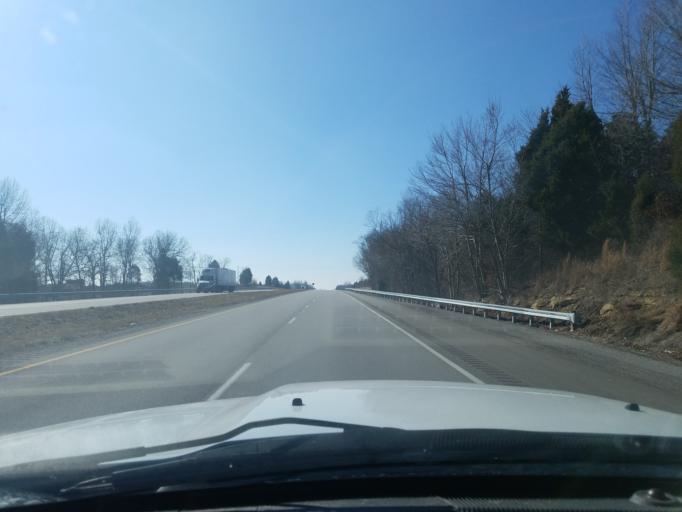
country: US
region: Kentucky
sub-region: Grayson County
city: Leitchfield
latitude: 37.5420
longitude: -86.1293
